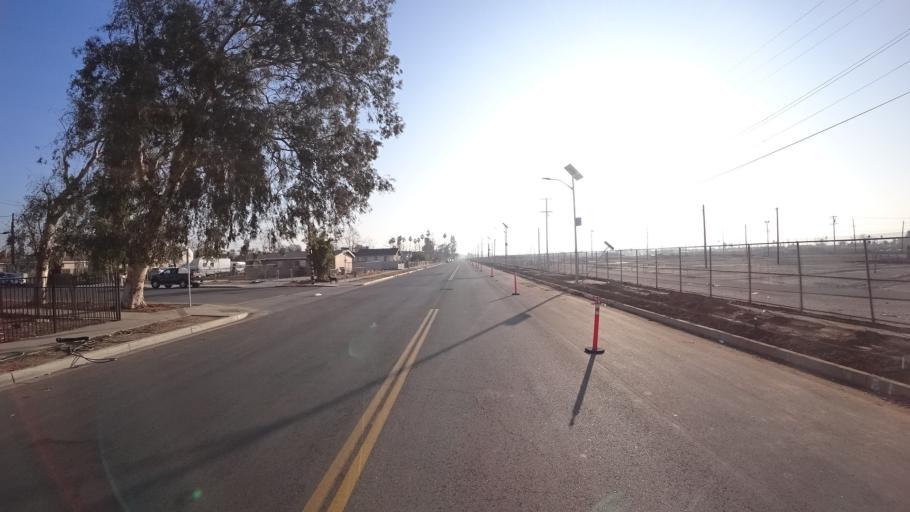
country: US
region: California
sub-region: Kern County
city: Bakersfield
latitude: 35.3774
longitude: -118.9862
